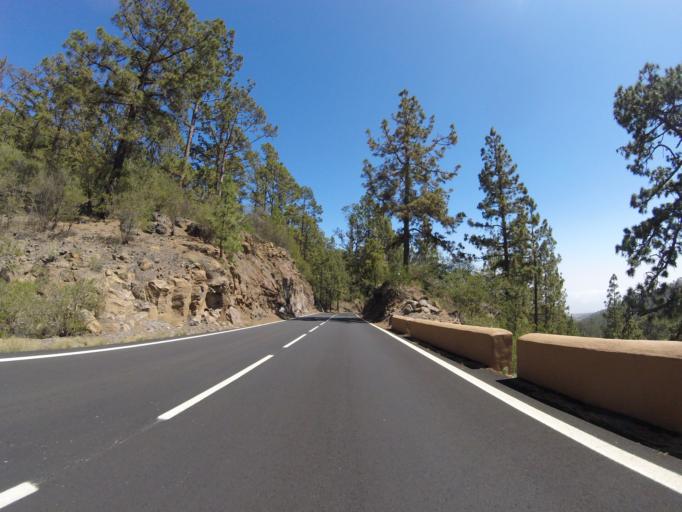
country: ES
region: Canary Islands
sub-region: Provincia de Santa Cruz de Tenerife
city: Vilaflor
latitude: 28.1732
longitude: -16.6376
